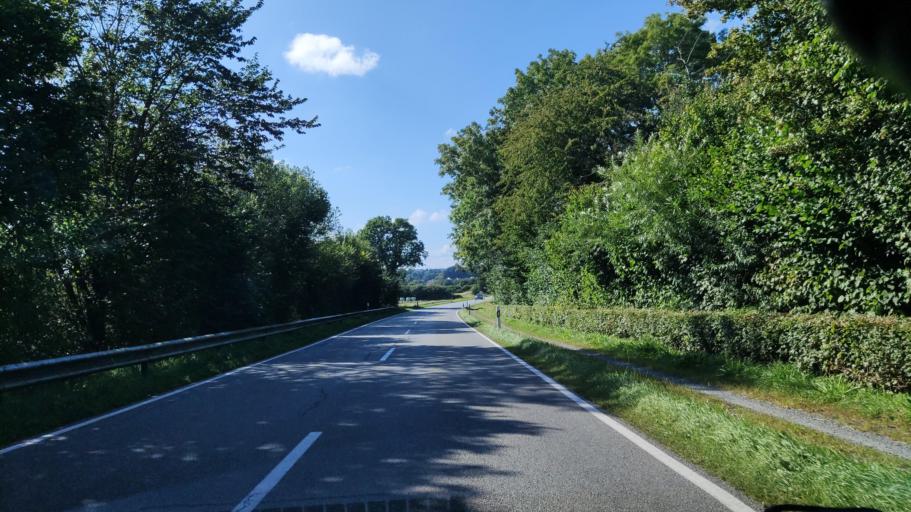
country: DE
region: Schleswig-Holstein
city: Hutten
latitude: 54.4309
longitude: 9.7214
